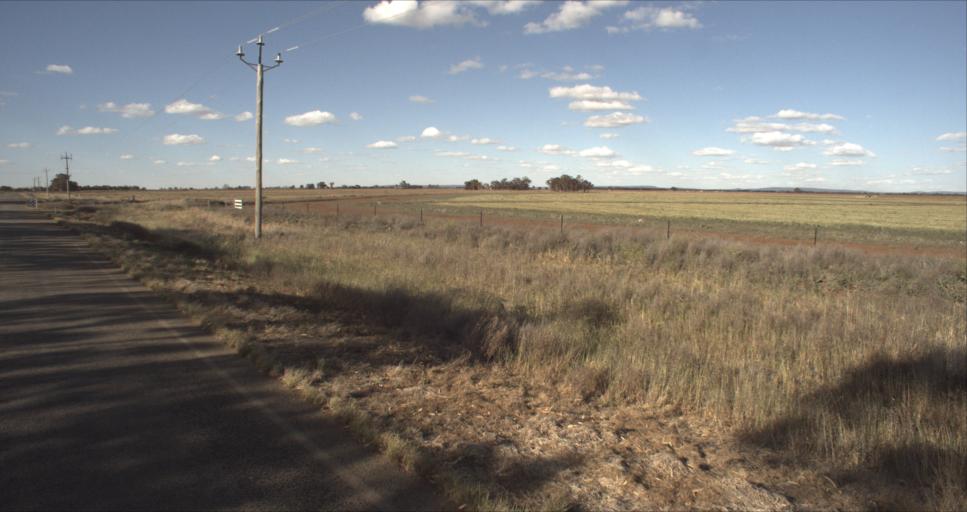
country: AU
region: New South Wales
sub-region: Leeton
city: Leeton
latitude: -34.5420
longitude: 146.2798
